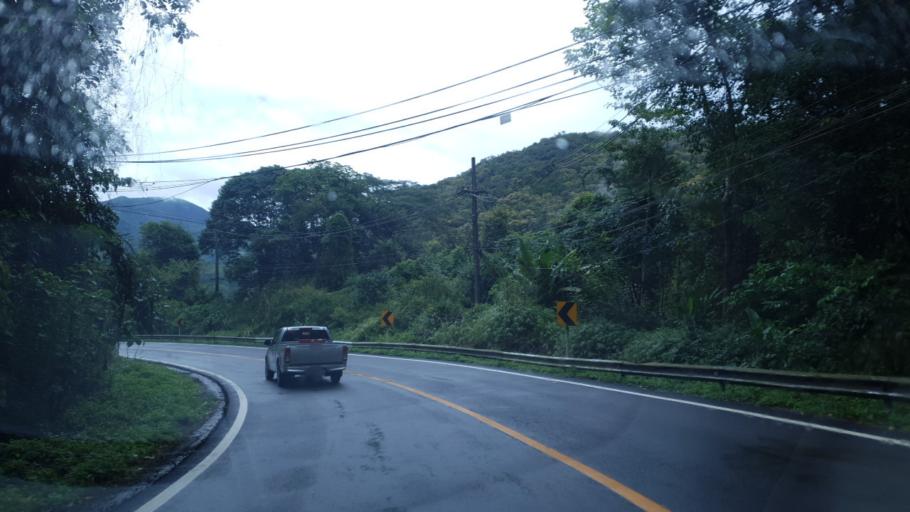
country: TH
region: Mae Hong Son
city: Ban Huai I Huak
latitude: 18.1415
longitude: 98.0918
